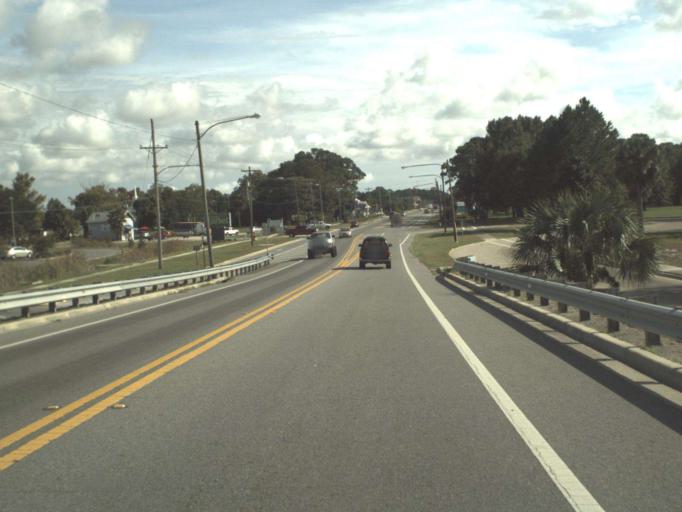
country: US
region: Florida
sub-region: Gulf County
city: Port Saint Joe
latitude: 29.8218
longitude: -85.3076
